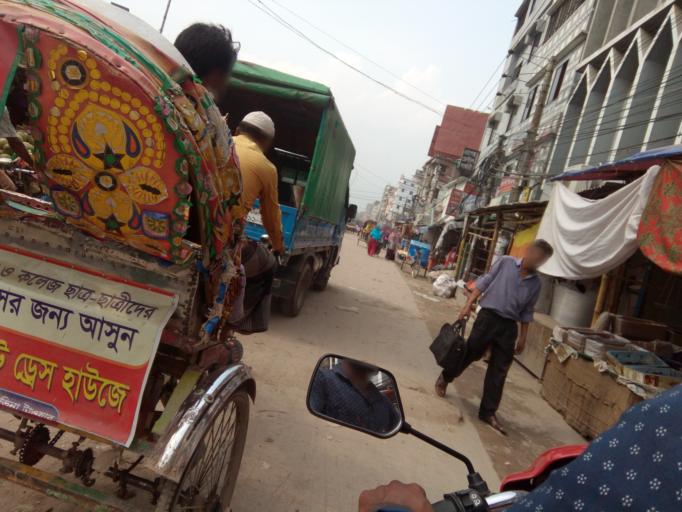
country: BD
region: Dhaka
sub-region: Dhaka
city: Dhaka
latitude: 23.7044
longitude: 90.4509
